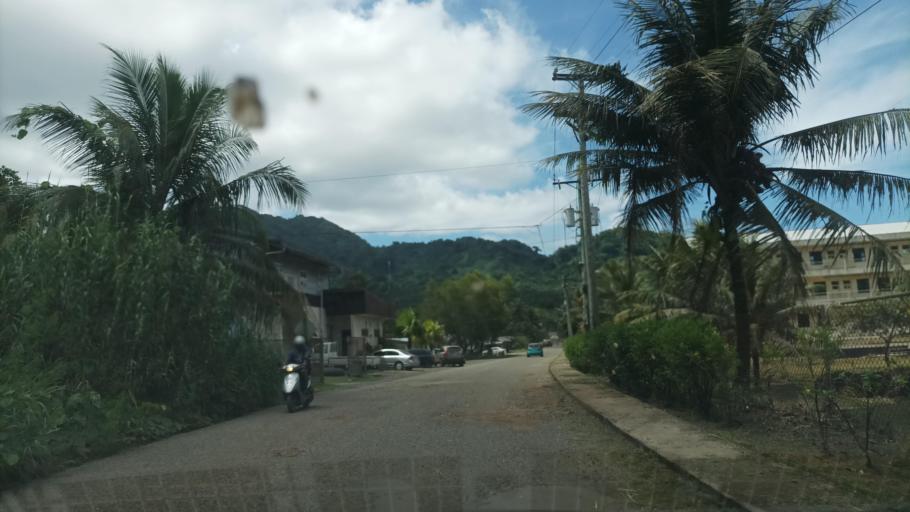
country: FM
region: Kosrae
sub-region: Lelu Municipality
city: Tofol
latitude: 5.3258
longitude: 163.0086
